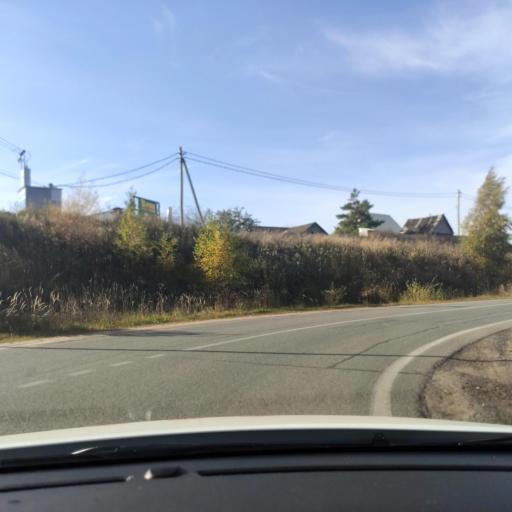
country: RU
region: Tatarstan
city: Vysokaya Gora
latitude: 55.7451
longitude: 49.3970
